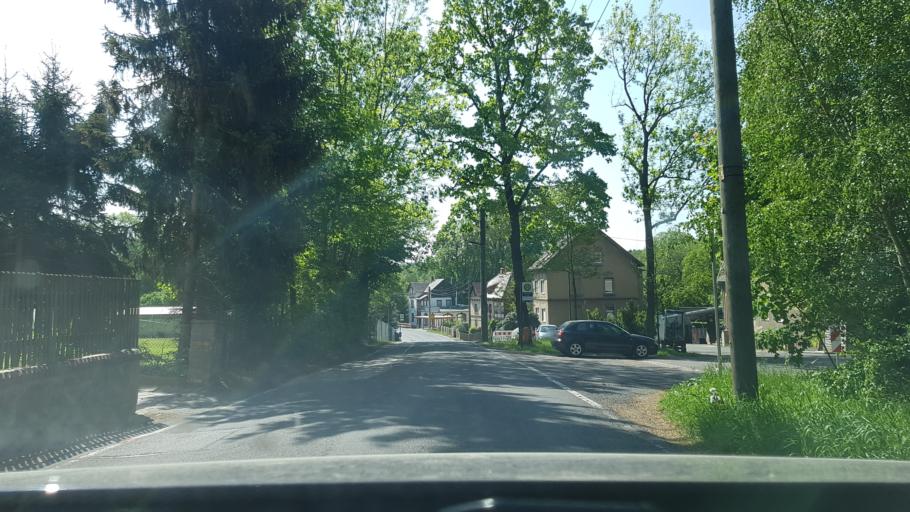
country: DE
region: Saxony
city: Wittgensdorf
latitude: 50.8716
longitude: 12.8746
